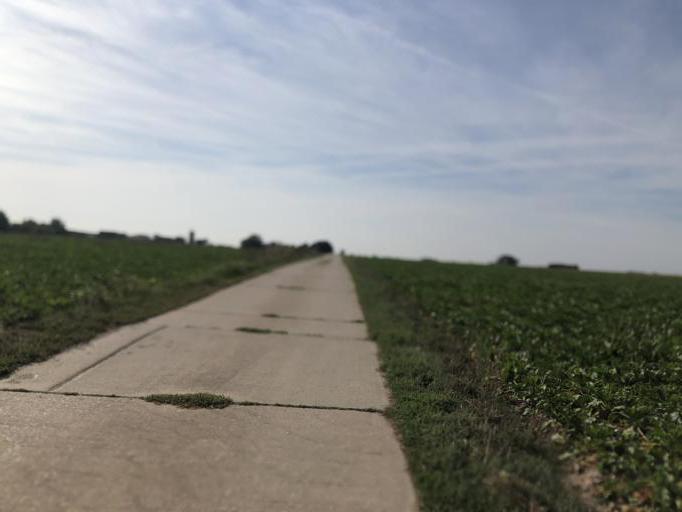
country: DE
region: Bavaria
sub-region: Regierungsbezirk Mittelfranken
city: Obermichelbach
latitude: 49.5454
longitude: 10.9558
